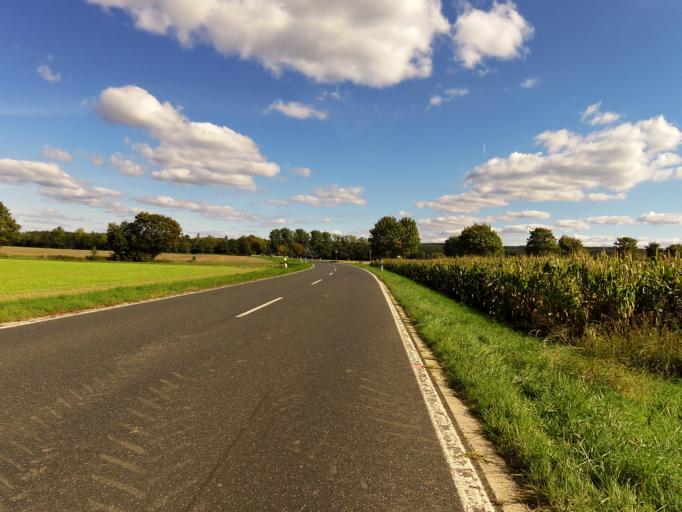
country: DE
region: North Rhine-Westphalia
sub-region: Regierungsbezirk Koln
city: Euskirchen
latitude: 50.6214
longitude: 6.8616
